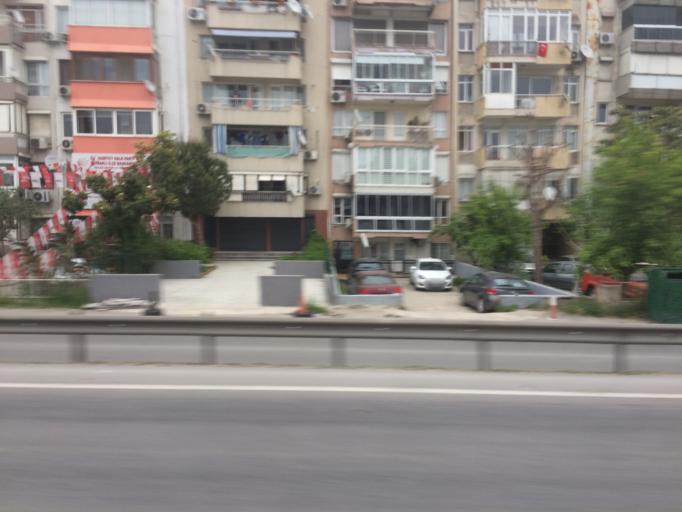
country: TR
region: Izmir
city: Karsiyaka
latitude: 38.4659
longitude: 27.1612
